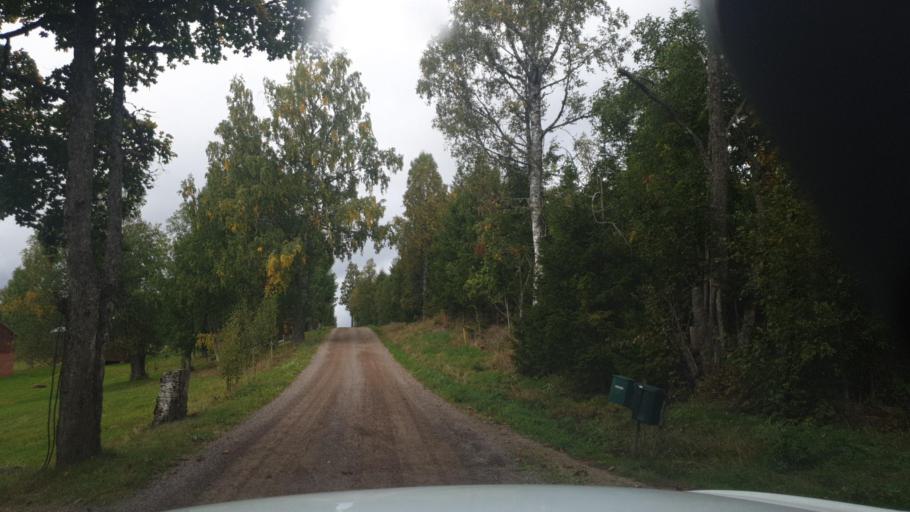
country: SE
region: Vaermland
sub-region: Torsby Kommun
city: Torsby
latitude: 59.9444
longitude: 12.7984
